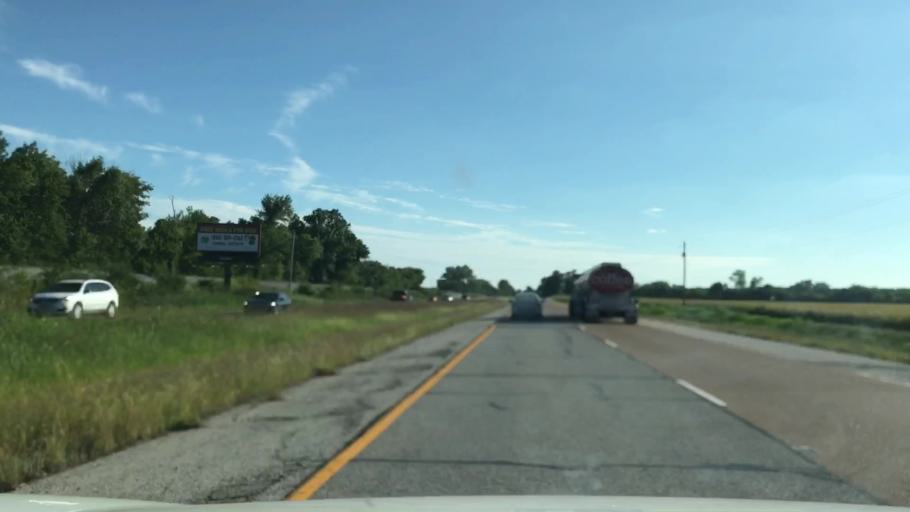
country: US
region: Illinois
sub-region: Madison County
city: Mitchell
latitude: 38.7926
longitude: -90.1038
